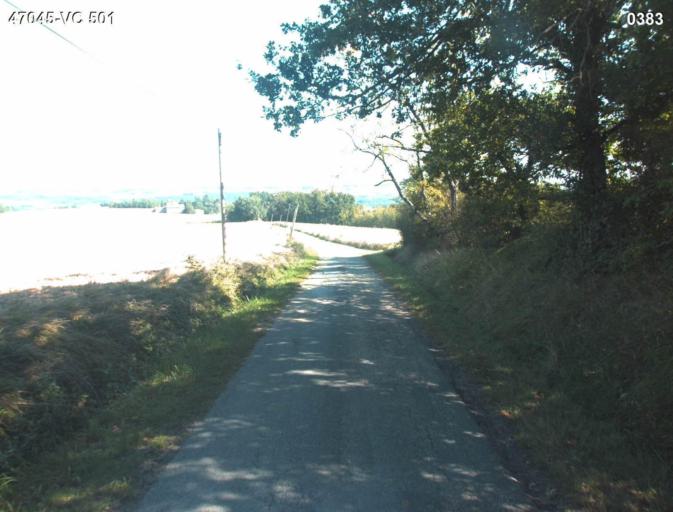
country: FR
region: Aquitaine
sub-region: Departement du Lot-et-Garonne
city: Nerac
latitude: 44.1547
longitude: 0.4047
